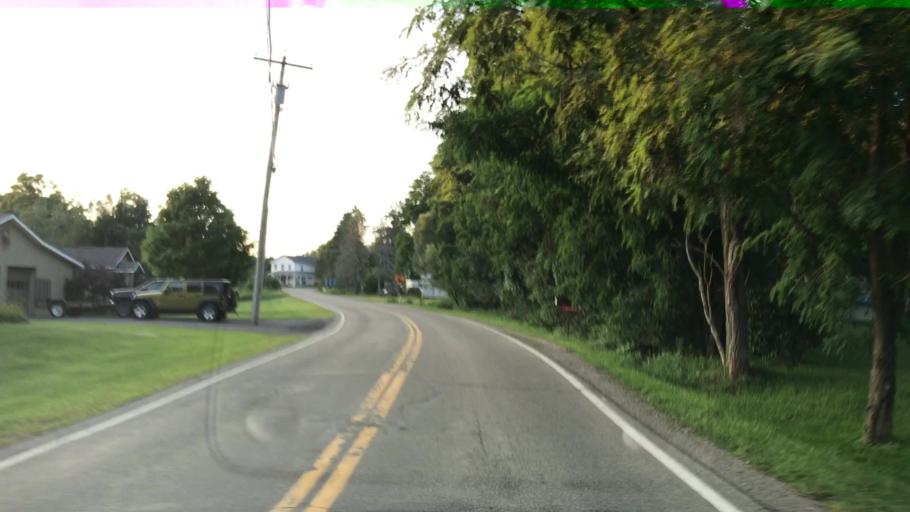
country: US
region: New York
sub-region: Chautauqua County
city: Mayville
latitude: 42.2656
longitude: -79.4712
